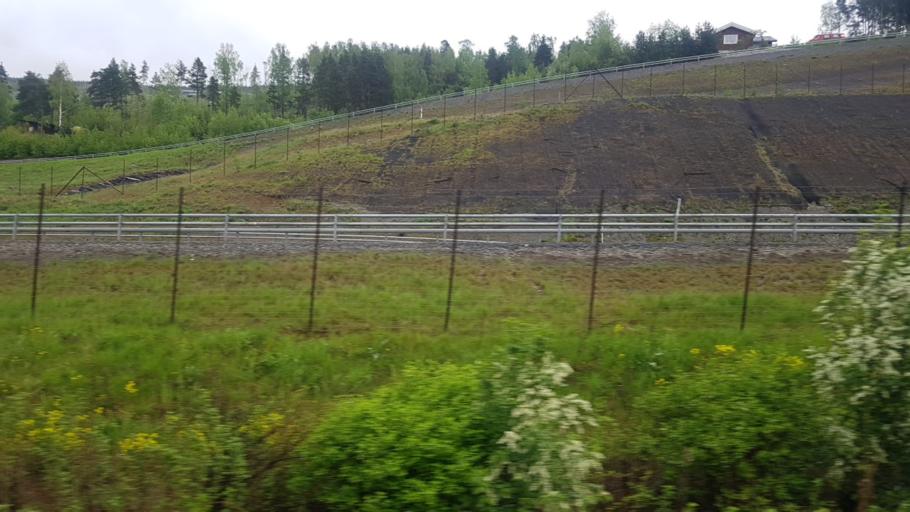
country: NO
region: Oppland
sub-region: Sor-Fron
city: Hundorp
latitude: 61.5562
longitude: 9.9445
